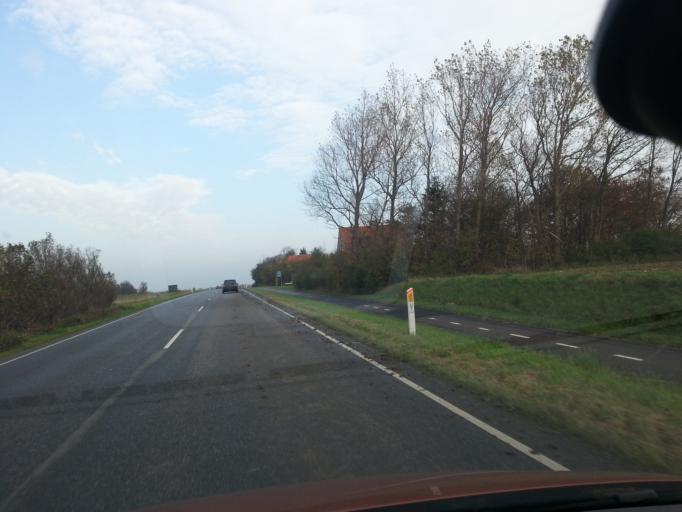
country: DK
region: Zealand
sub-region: Guldborgsund Kommune
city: Nykobing Falster
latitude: 54.5888
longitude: 11.9302
